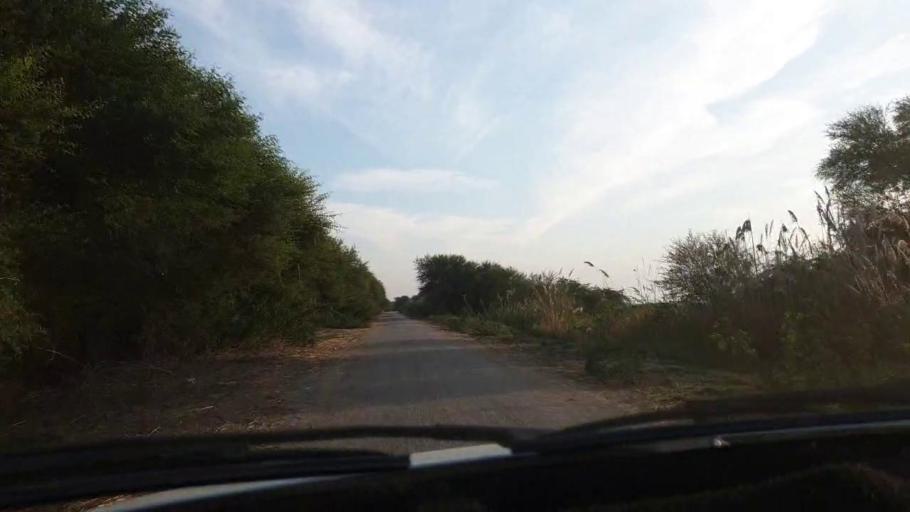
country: PK
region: Sindh
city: Bulri
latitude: 25.0176
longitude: 68.2890
